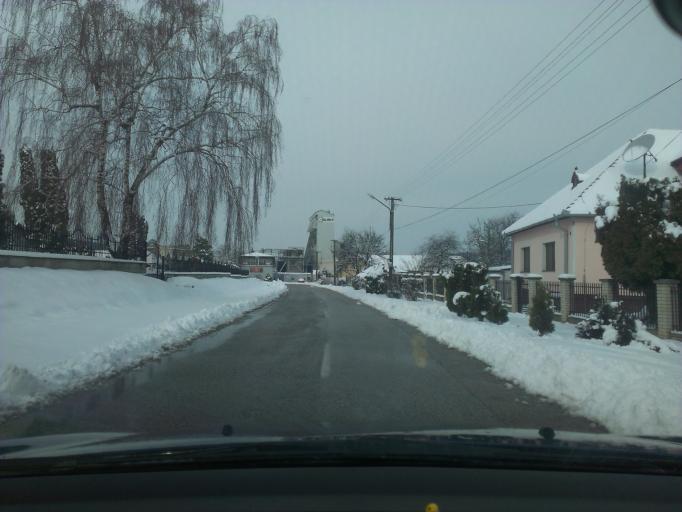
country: SK
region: Nitriansky
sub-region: Okres Nitra
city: Nitra
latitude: 48.3821
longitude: 18.1688
